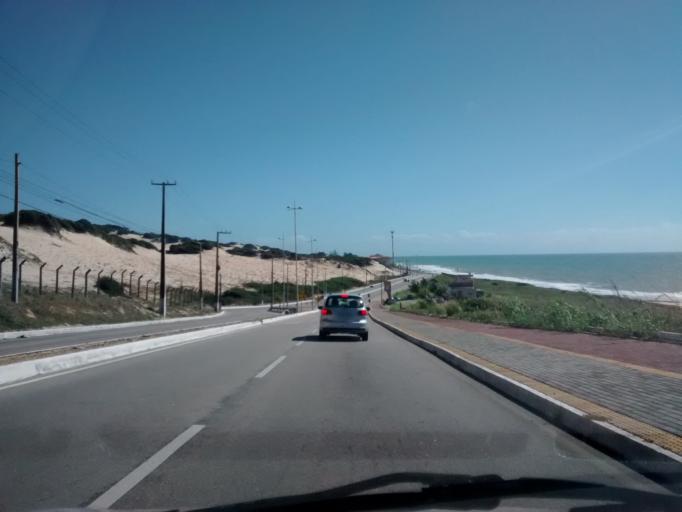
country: BR
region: Rio Grande do Norte
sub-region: Natal
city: Natal
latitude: -5.8182
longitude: -35.1832
